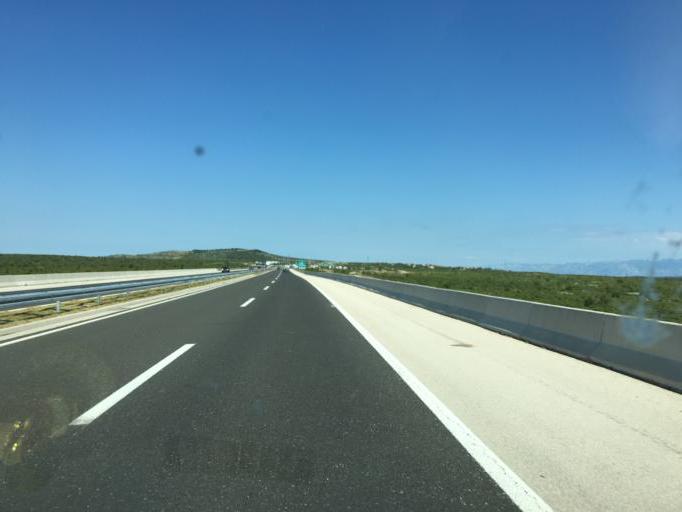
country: HR
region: Zadarska
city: Polaca
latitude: 44.0558
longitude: 15.5401
